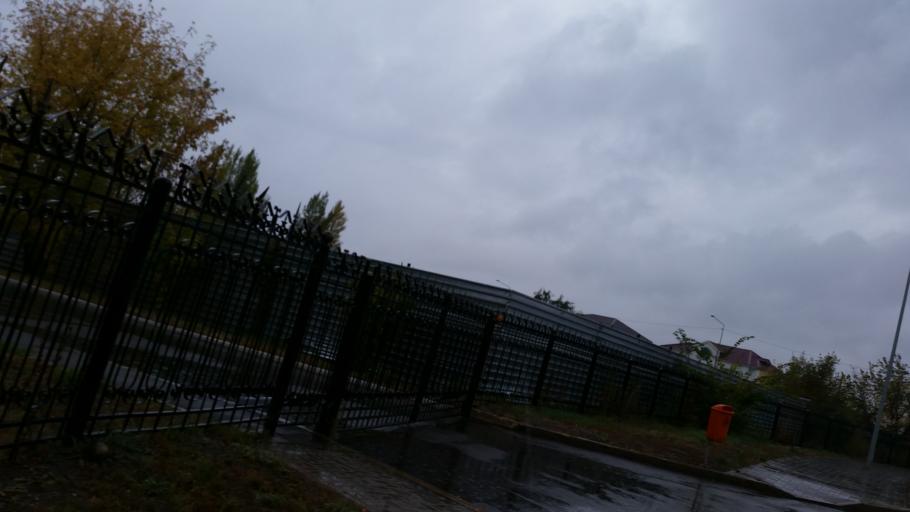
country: KZ
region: Astana Qalasy
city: Astana
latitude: 51.1505
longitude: 71.4935
